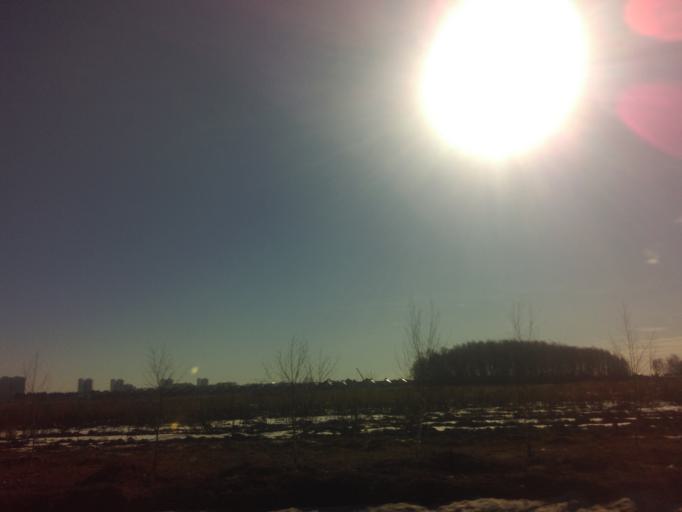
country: RU
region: Moskovskaya
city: Kommunarka
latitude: 55.5415
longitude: 37.4735
